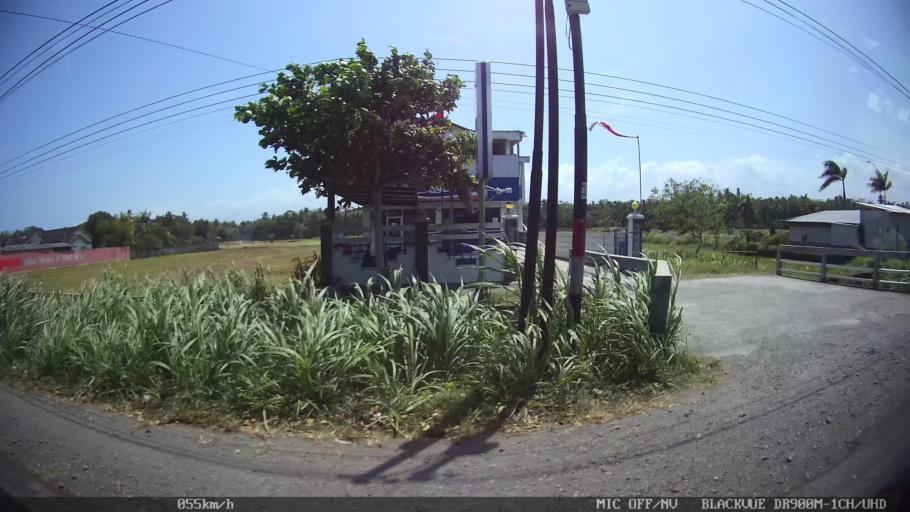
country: ID
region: Daerah Istimewa Yogyakarta
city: Srandakan
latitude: -7.9517
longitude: 110.2057
